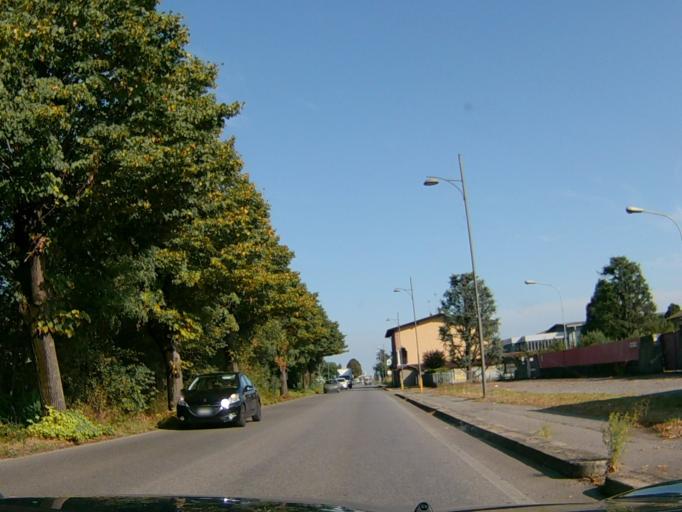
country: IT
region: Lombardy
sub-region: Provincia di Brescia
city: Cologne
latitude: 45.5774
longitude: 9.9390
